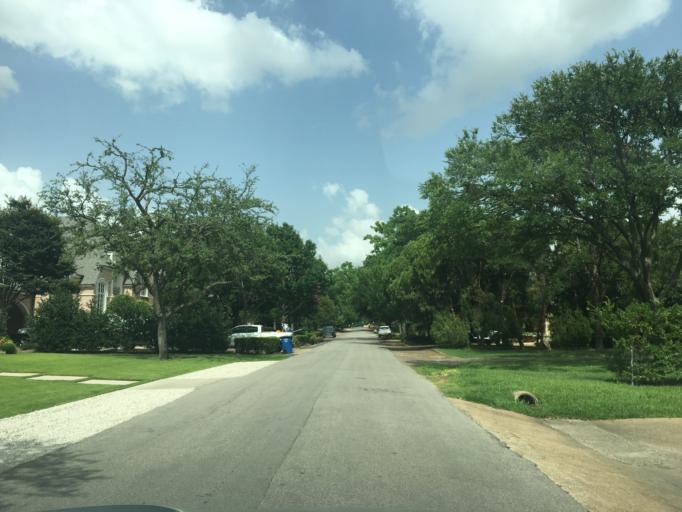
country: US
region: Texas
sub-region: Dallas County
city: University Park
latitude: 32.8843
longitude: -96.7964
